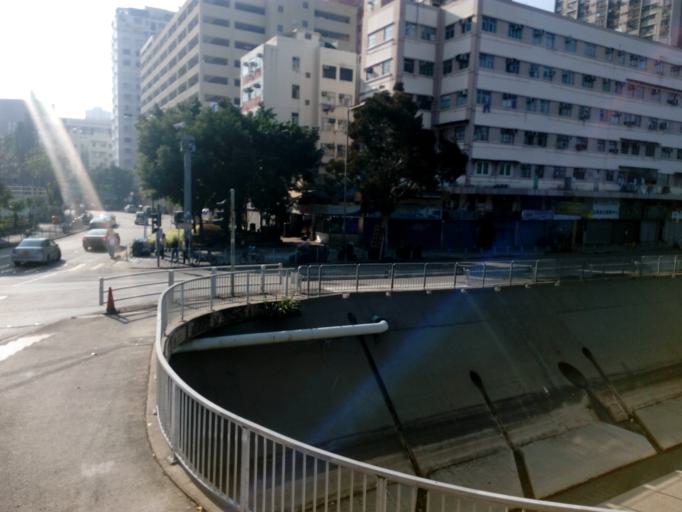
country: HK
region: Yuen Long
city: Yuen Long Kau Hui
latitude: 22.4476
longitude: 114.0218
